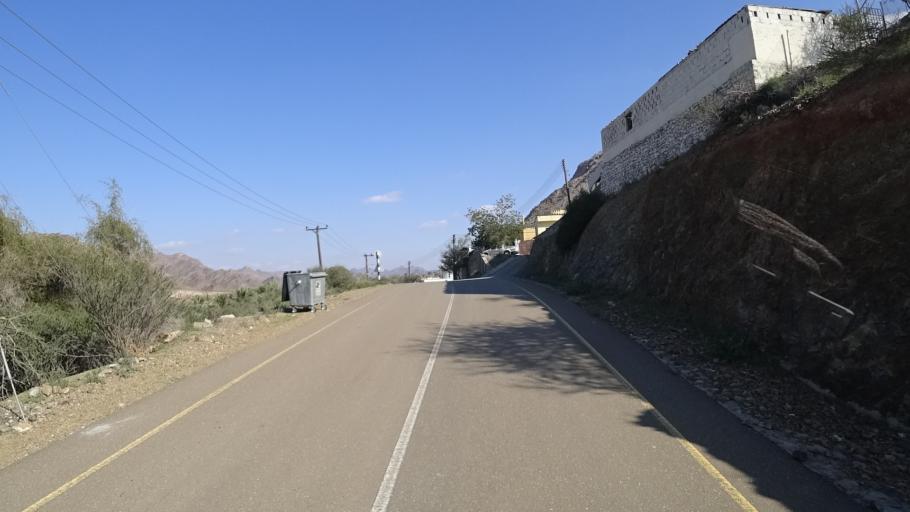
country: OM
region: Al Batinah
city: Rustaq
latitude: 23.4575
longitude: 57.0847
